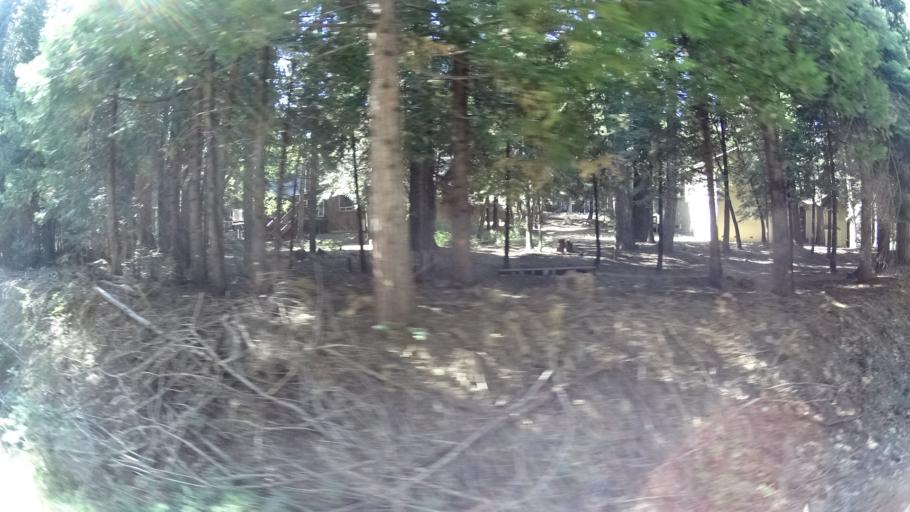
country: US
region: California
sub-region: Calaveras County
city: Arnold
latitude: 38.3000
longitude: -120.2689
